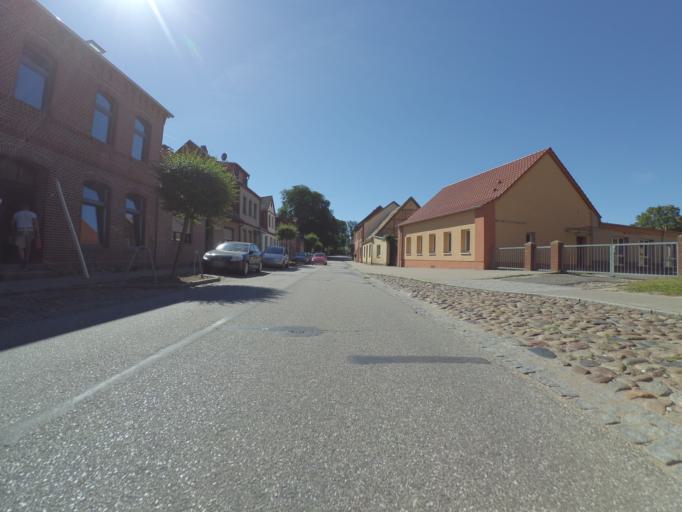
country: DE
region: Mecklenburg-Vorpommern
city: Plau am See
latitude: 53.4609
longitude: 12.2638
